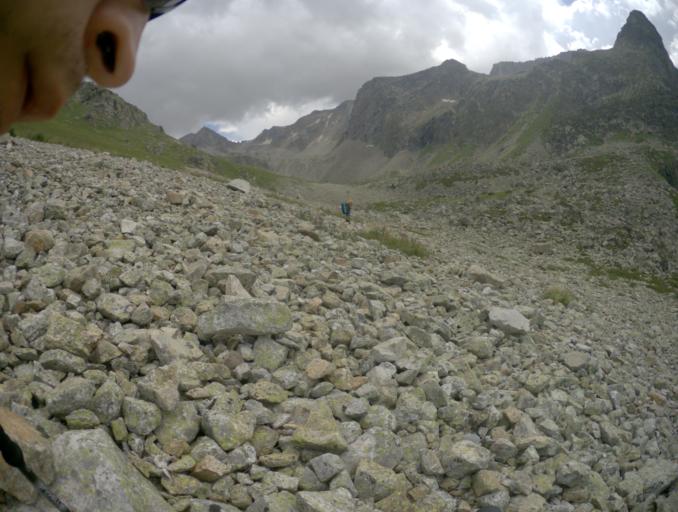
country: RU
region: Karachayevo-Cherkesiya
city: Uchkulan
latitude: 43.2905
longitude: 42.0801
